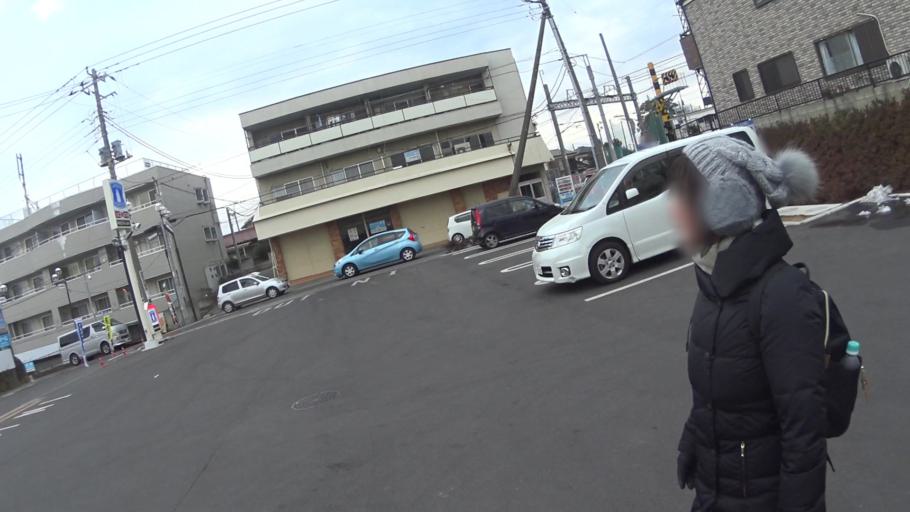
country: JP
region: Chiba
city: Funabashi
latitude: 35.7473
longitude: 139.9939
